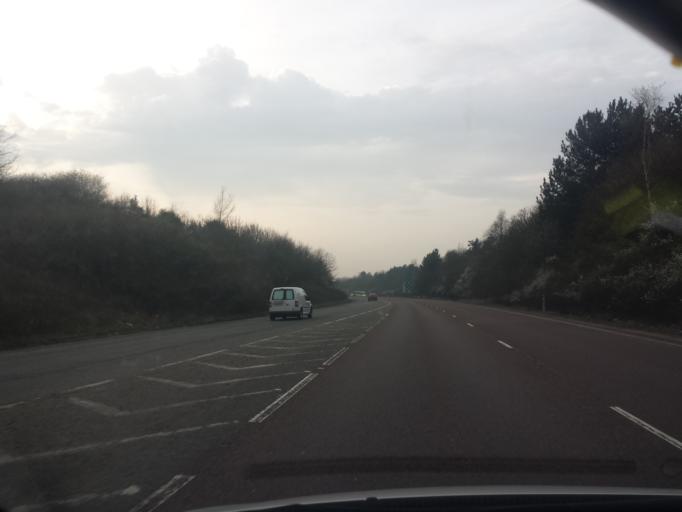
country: GB
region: England
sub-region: Essex
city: Colchester
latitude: 51.9232
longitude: 0.9305
